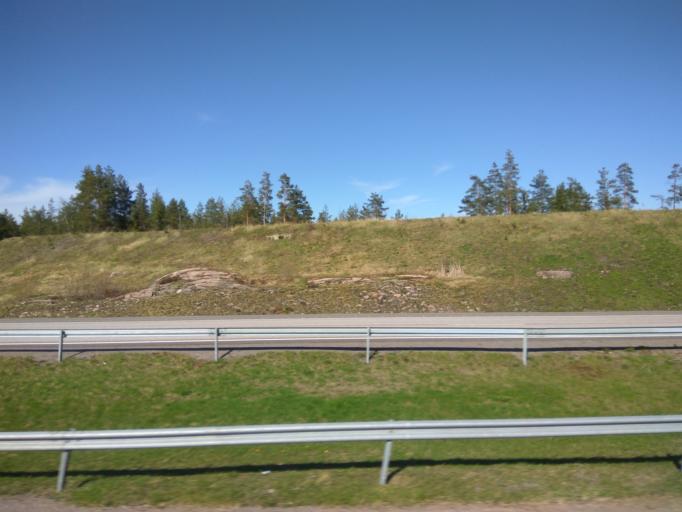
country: FI
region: Uusimaa
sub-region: Loviisa
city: Perna
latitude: 60.4820
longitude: 26.0257
